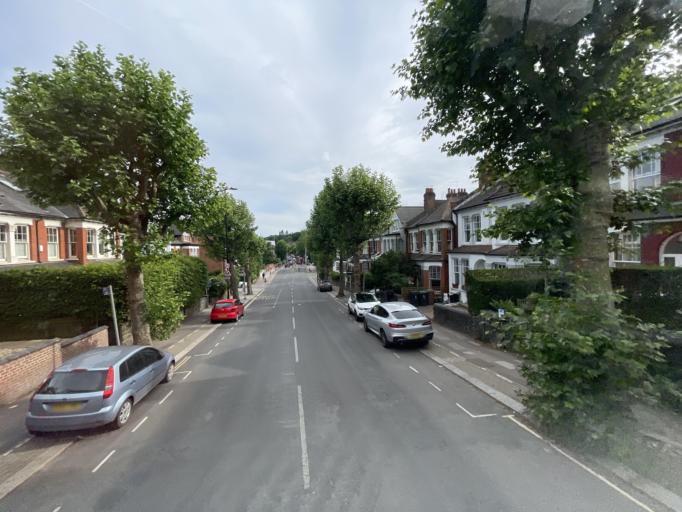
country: GB
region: England
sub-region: Greater London
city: Crouch End
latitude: 51.5876
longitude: -0.1469
